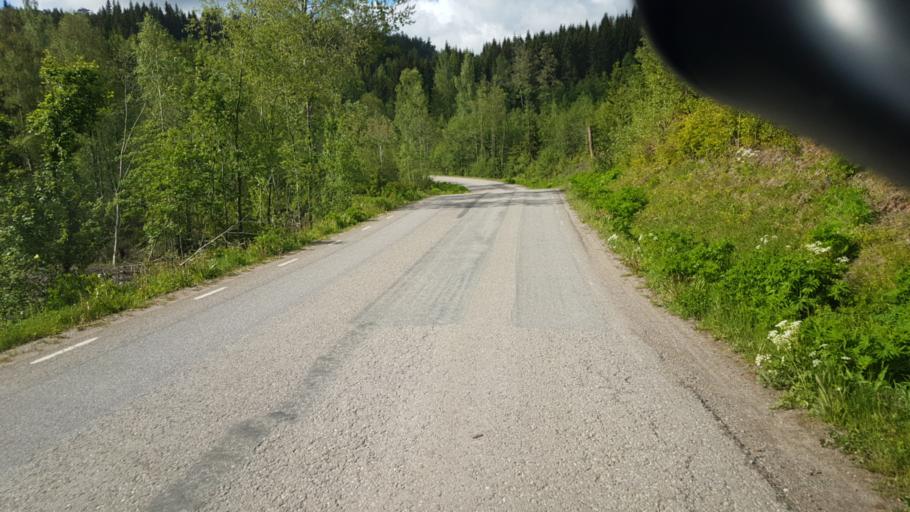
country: NO
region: Ostfold
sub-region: Romskog
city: Romskog
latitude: 59.8302
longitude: 11.9544
